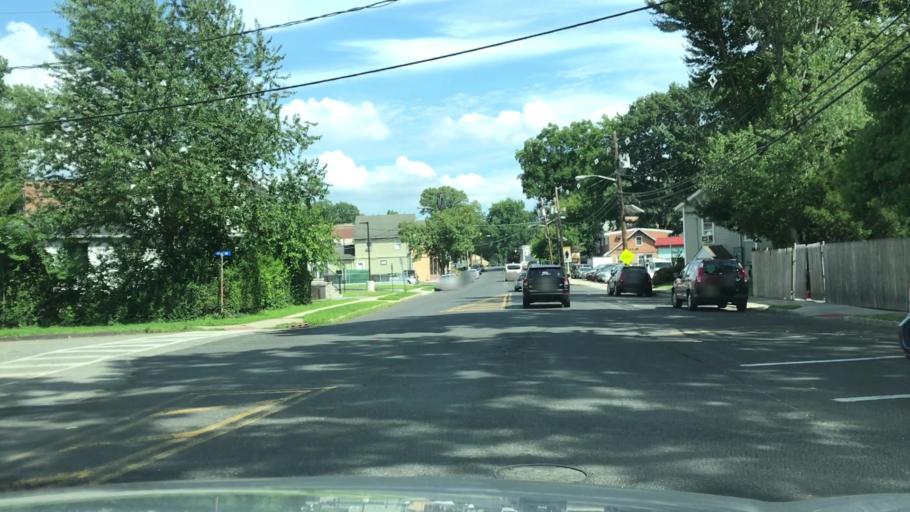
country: US
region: New Jersey
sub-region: Bergen County
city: Dumont
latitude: 40.9487
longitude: -73.9874
